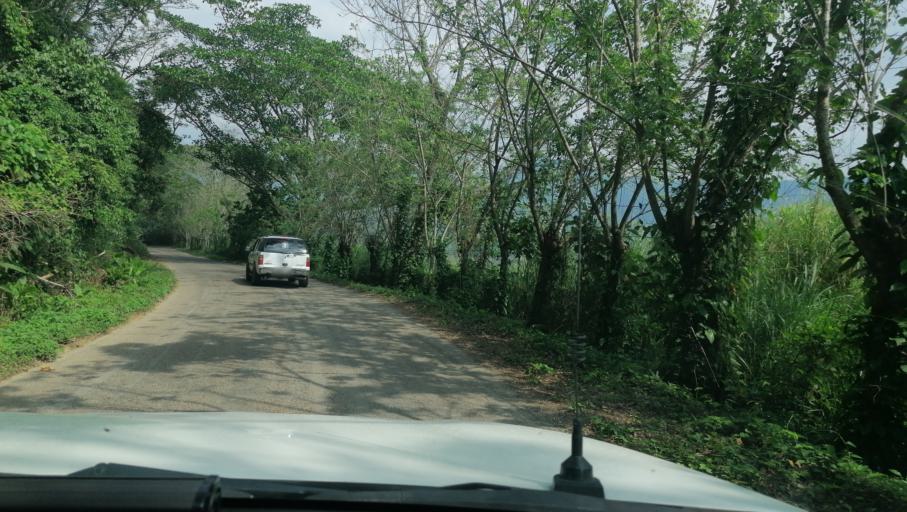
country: MX
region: Chiapas
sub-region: Francisco Leon
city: San Miguel la Sardina
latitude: 17.2274
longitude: -93.3478
